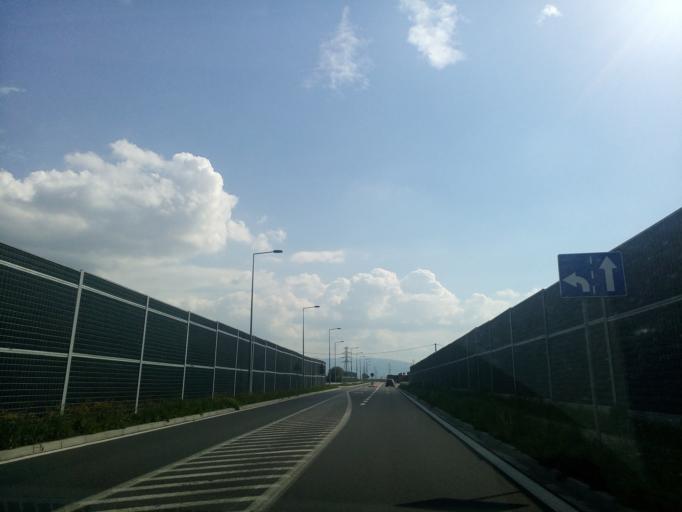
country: PL
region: Lesser Poland Voivodeship
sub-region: Powiat nowosadecki
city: Chelmiec
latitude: 49.6251
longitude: 20.6454
